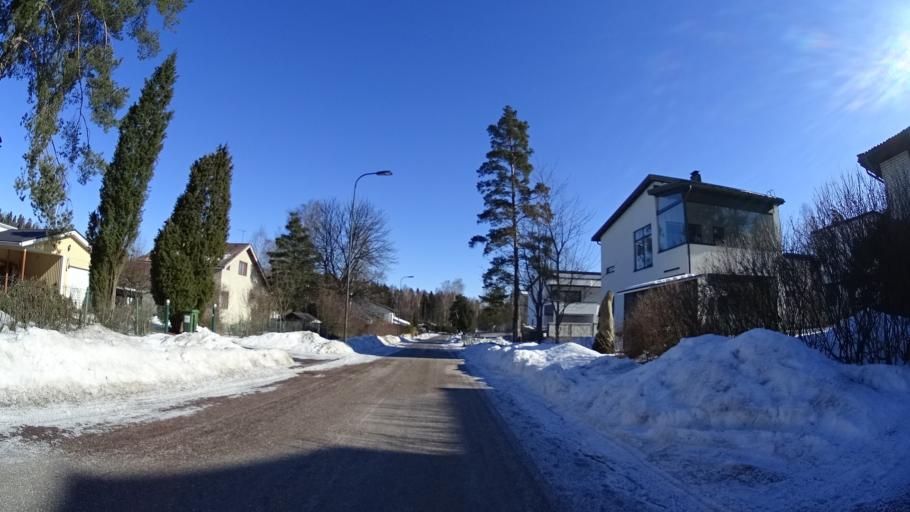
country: FI
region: Uusimaa
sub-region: Helsinki
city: Kilo
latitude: 60.1901
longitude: 24.7606
